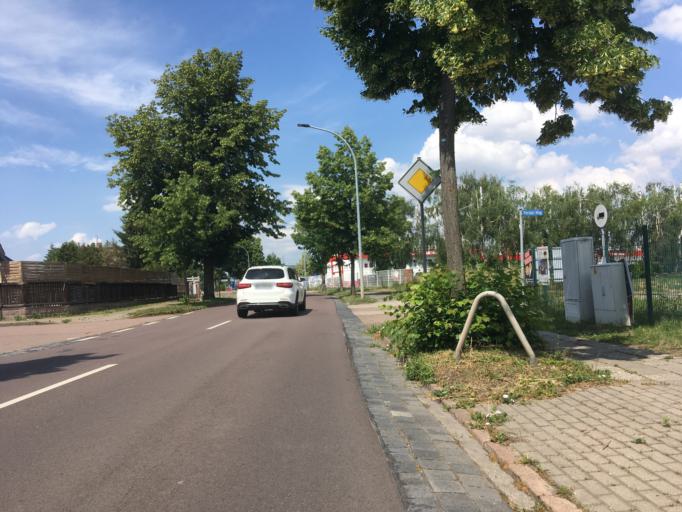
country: DE
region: Saxony-Anhalt
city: Koethen
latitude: 51.7541
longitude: 12.0039
